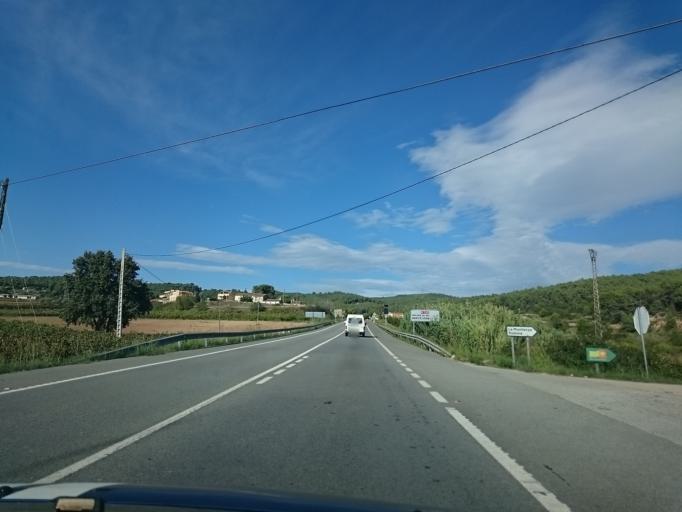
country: ES
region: Catalonia
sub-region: Provincia de Barcelona
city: Subirats
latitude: 41.3820
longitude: 1.8116
